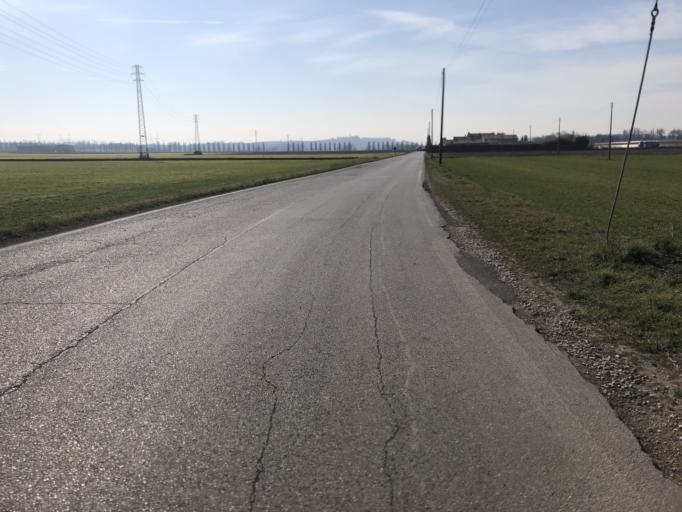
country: IT
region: Veneto
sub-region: Provincia di Verona
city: San Giorgio in Salici
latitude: 45.4129
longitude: 10.8007
